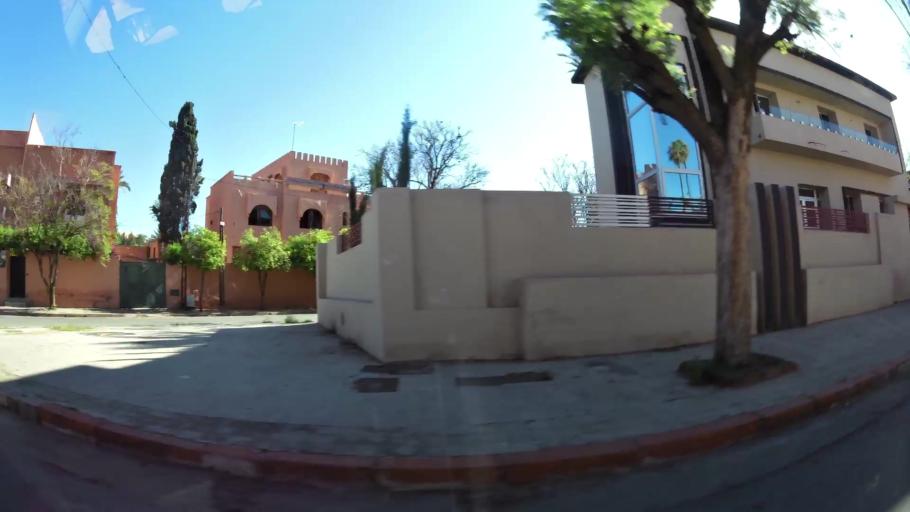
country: MA
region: Marrakech-Tensift-Al Haouz
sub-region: Marrakech
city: Marrakesh
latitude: 31.6398
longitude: -8.0147
